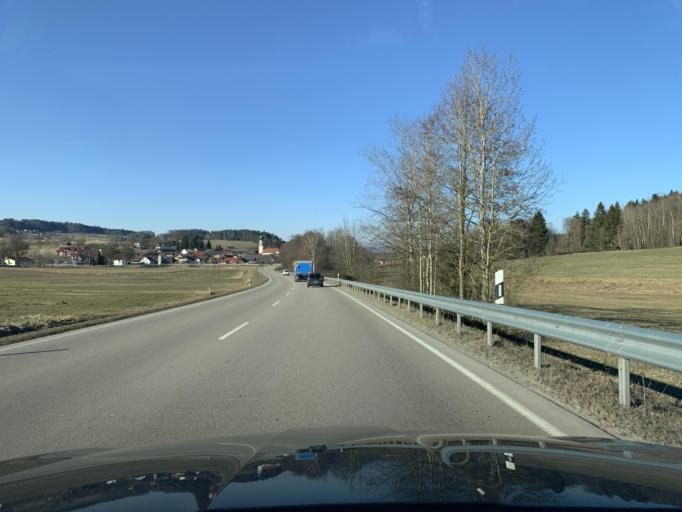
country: DE
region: Bavaria
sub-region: Upper Palatinate
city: Pemfling
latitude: 49.2962
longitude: 12.6295
